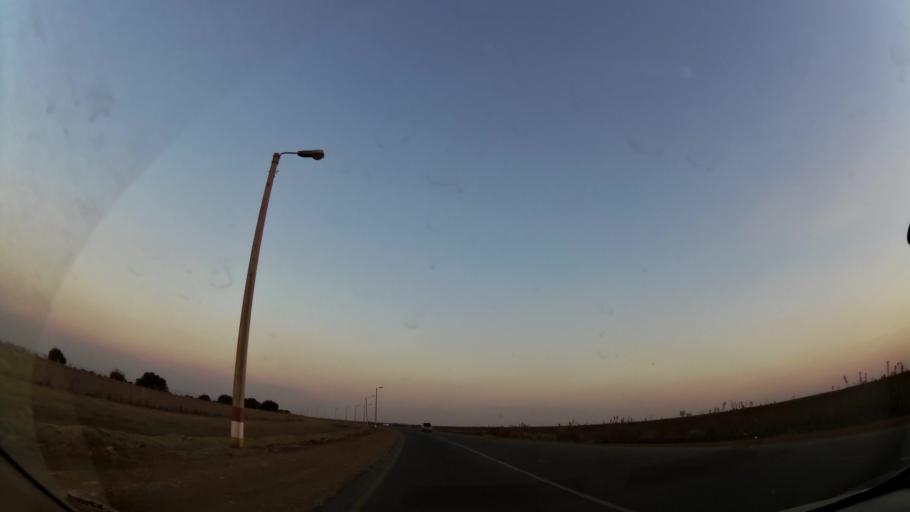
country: ZA
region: Gauteng
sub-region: Ekurhuleni Metropolitan Municipality
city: Nigel
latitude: -26.3542
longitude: 28.4132
